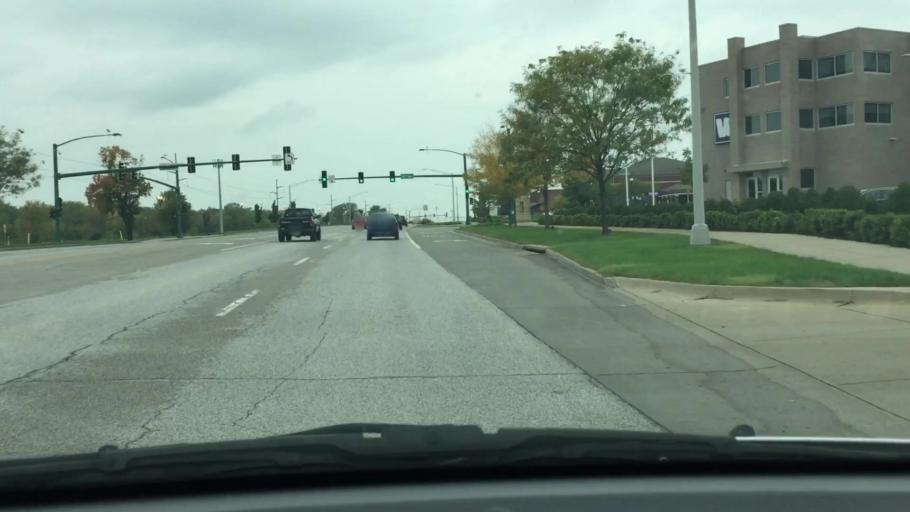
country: US
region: Iowa
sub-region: Johnson County
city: Coralville
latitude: 41.6727
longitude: -91.5777
